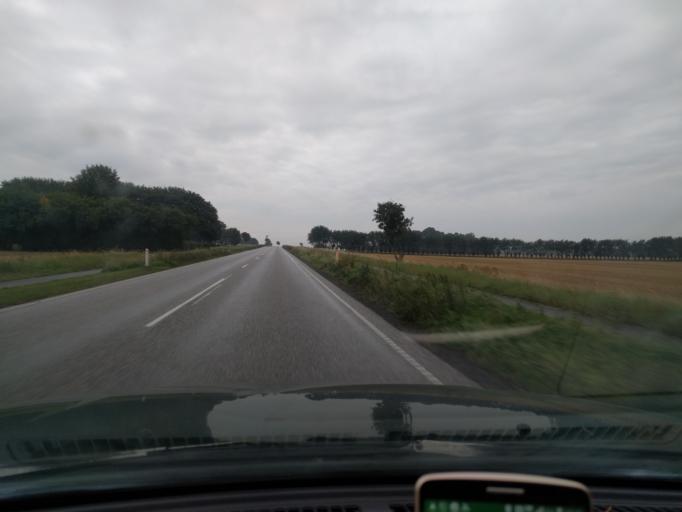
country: DK
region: Zealand
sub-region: Naestved Kommune
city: Naestved
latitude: 55.1688
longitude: 11.8124
